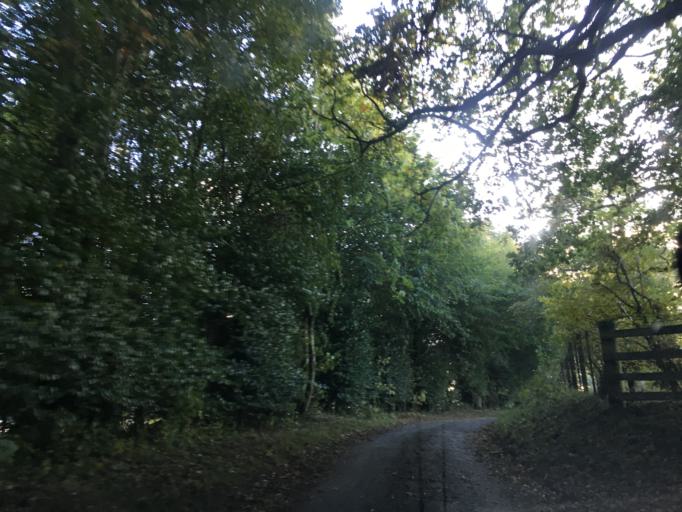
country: GB
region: Scotland
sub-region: East Lothian
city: Pencaitland
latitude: 55.8595
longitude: -2.9060
